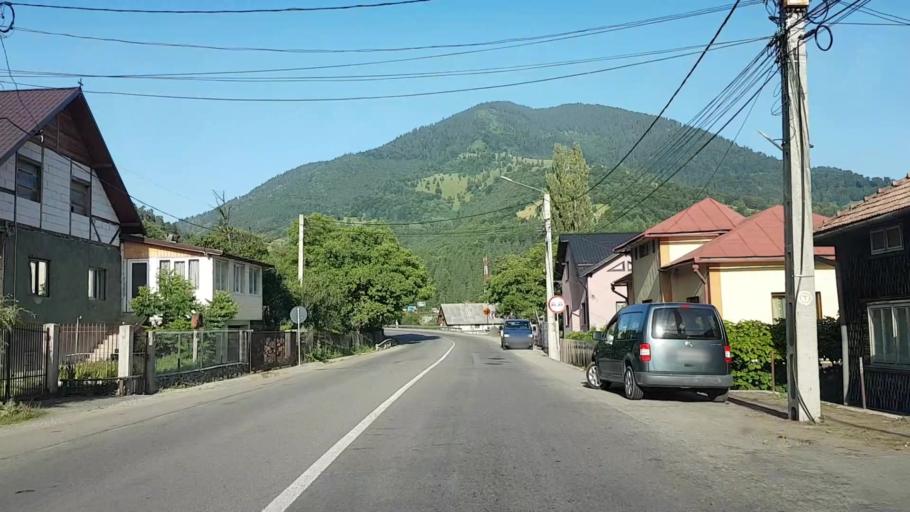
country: RO
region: Bistrita-Nasaud
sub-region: Comuna Tiha Bargaului
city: Tureac
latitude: 47.2098
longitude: 24.8635
